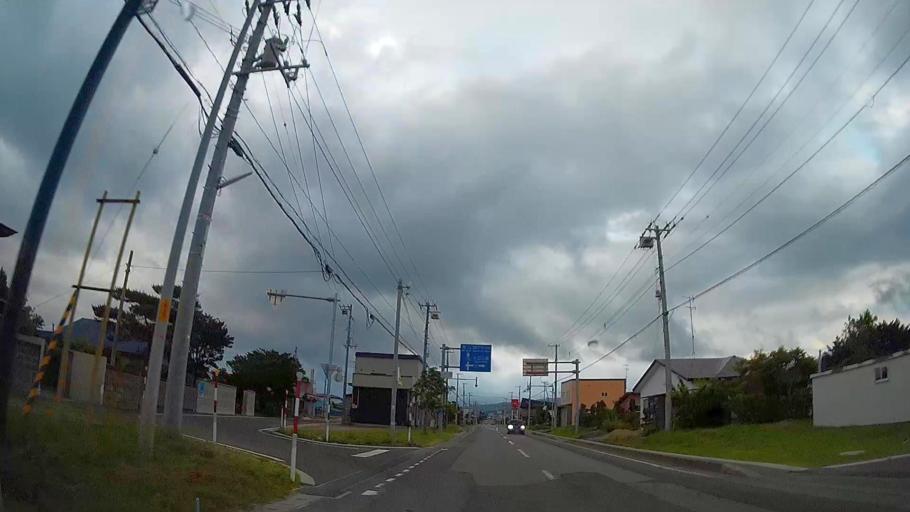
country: JP
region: Hokkaido
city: Nanae
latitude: 42.0445
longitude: 140.8109
